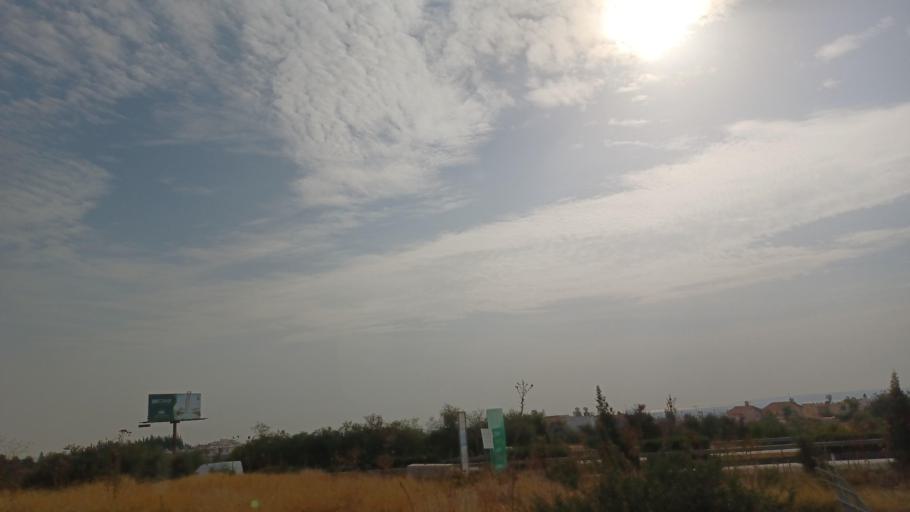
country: CY
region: Limassol
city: Ypsonas
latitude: 34.6959
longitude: 32.9497
